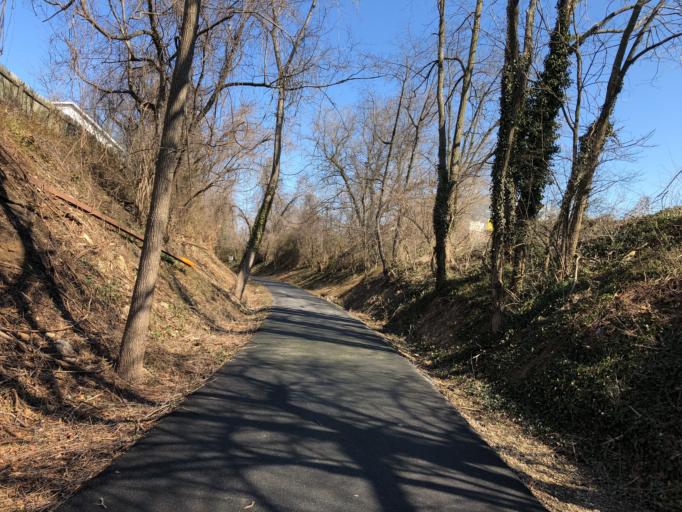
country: US
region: Maryland
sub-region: Kent County
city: Chestertown
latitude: 39.2163
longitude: -76.0714
